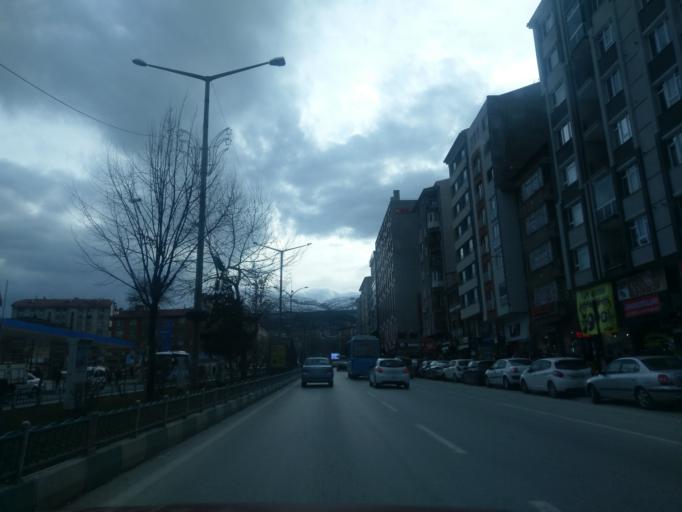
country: TR
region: Kuetahya
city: Kutahya
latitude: 39.4219
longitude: 29.9872
